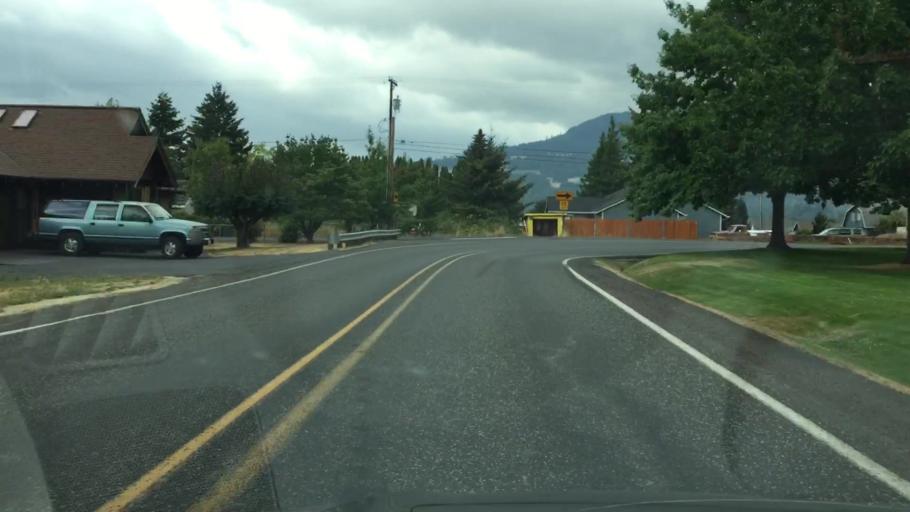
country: US
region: Washington
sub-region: Klickitat County
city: White Salmon
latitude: 45.7354
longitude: -121.5118
